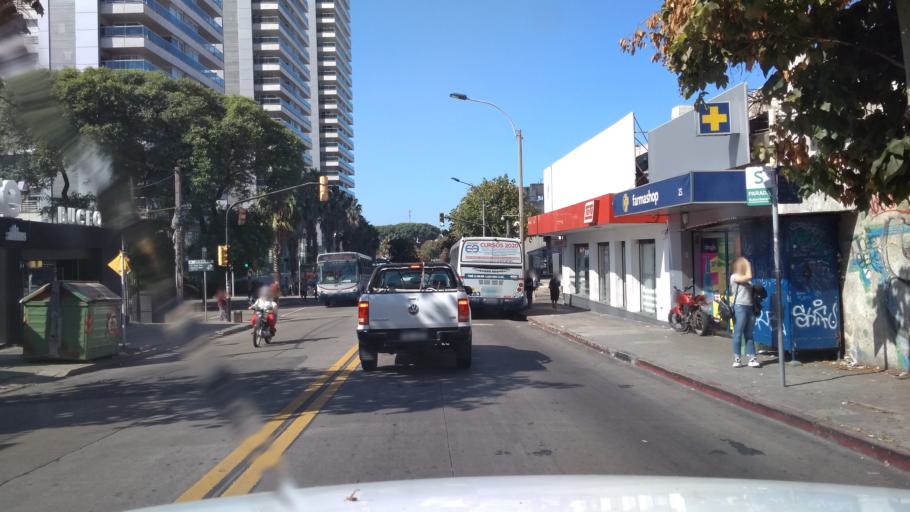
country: UY
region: Montevideo
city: Montevideo
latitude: -34.8961
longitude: -56.1220
